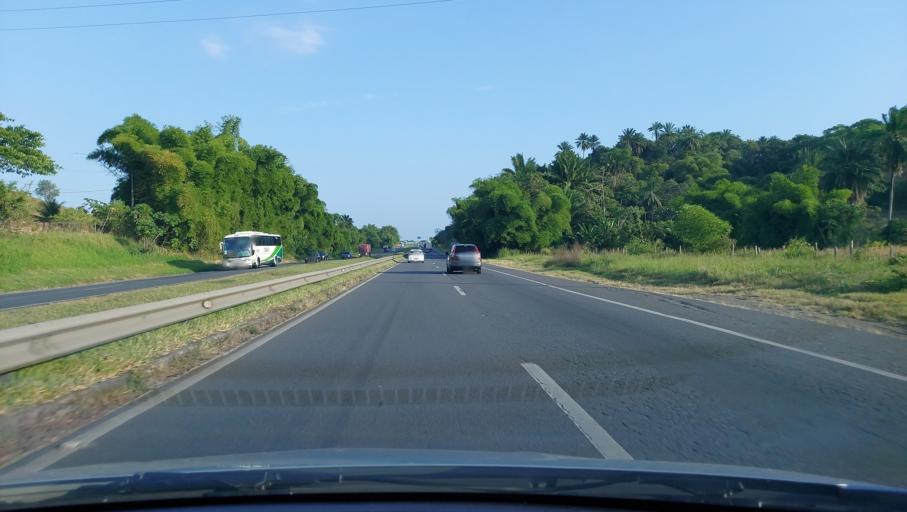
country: BR
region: Bahia
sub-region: Santo Amaro
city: Santo Amaro
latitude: -12.4428
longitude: -38.7197
